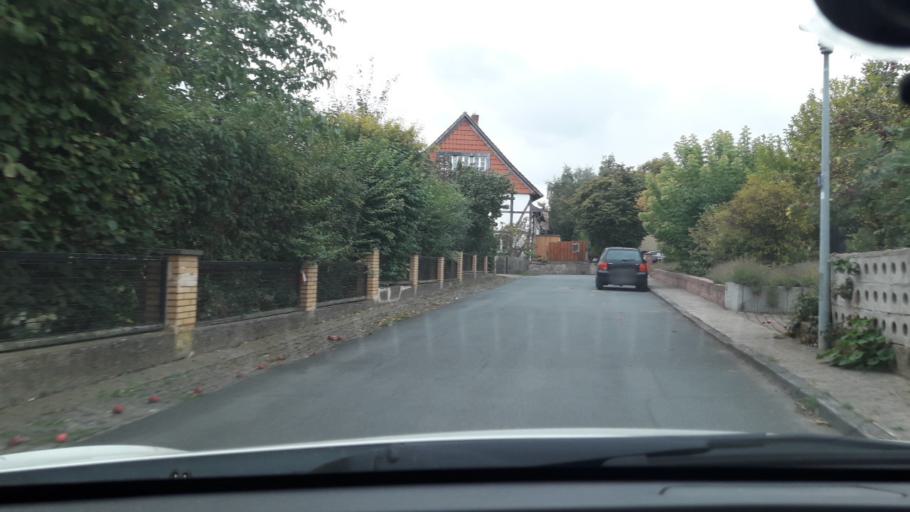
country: DE
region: Lower Saxony
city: Gielde
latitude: 52.0371
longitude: 10.4931
